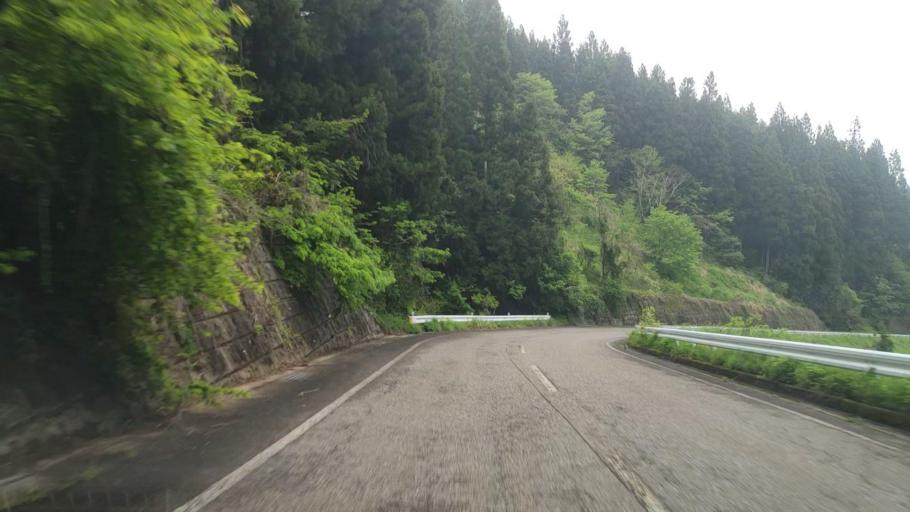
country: JP
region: Niigata
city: Gosen
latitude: 37.7151
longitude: 139.1164
